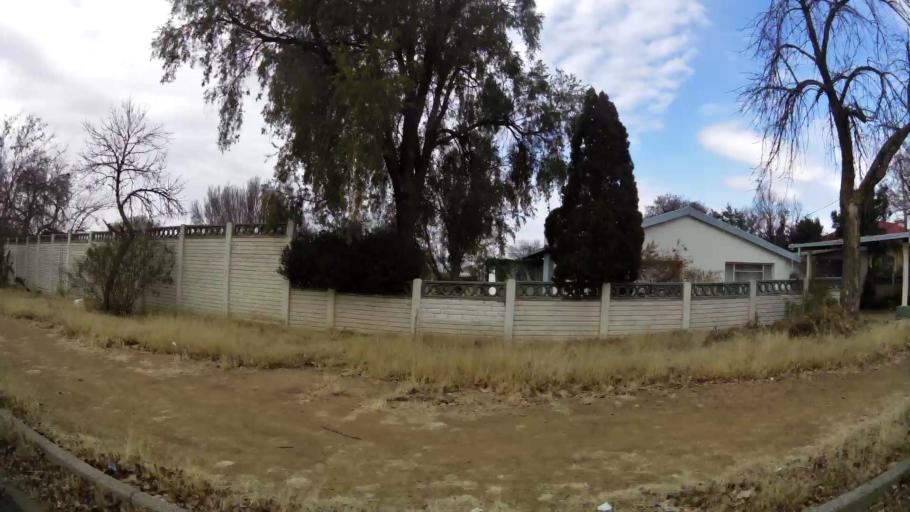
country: ZA
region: Orange Free State
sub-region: Fezile Dabi District Municipality
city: Kroonstad
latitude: -27.6345
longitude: 27.2261
